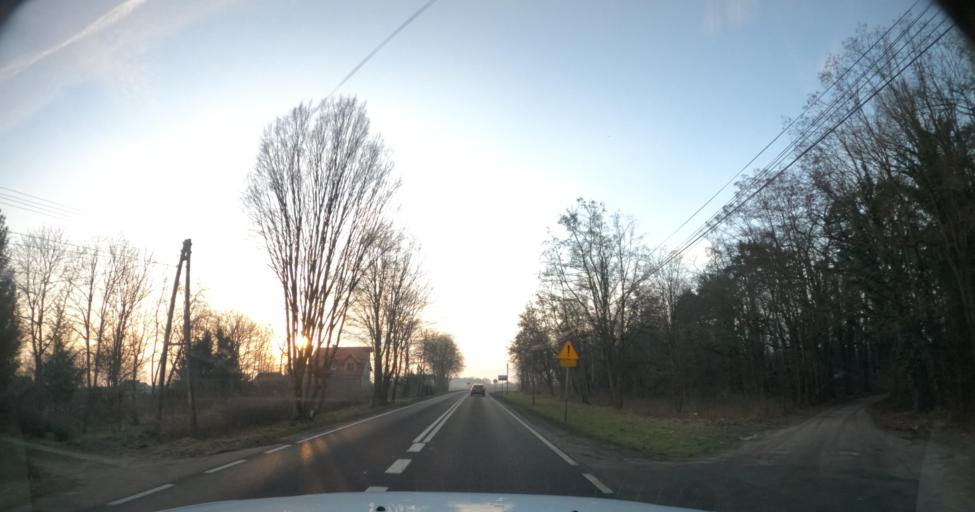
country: PL
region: West Pomeranian Voivodeship
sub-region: Powiat mysliborski
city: Mysliborz
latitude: 52.9091
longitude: 14.8556
